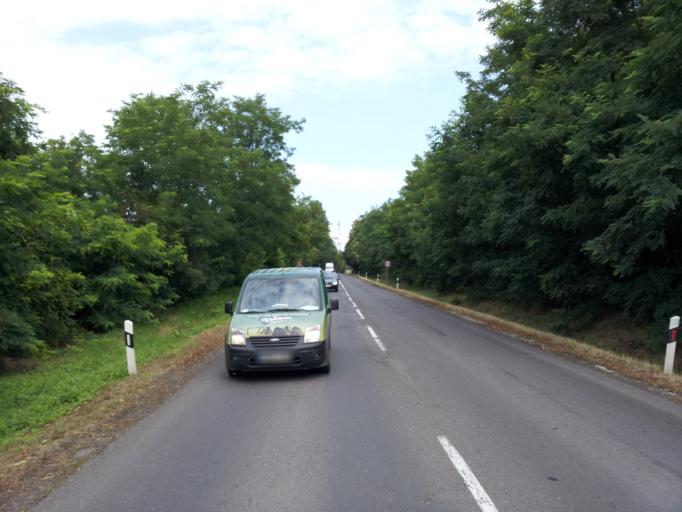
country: HU
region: Pest
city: Kiskunlachaza
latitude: 47.2386
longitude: 19.0206
